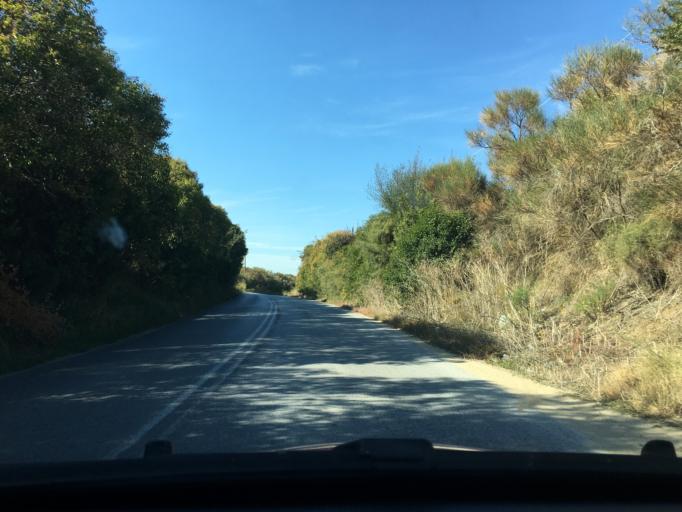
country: GR
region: Central Macedonia
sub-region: Nomos Chalkidikis
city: Nea Roda
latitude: 40.3810
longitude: 23.9077
